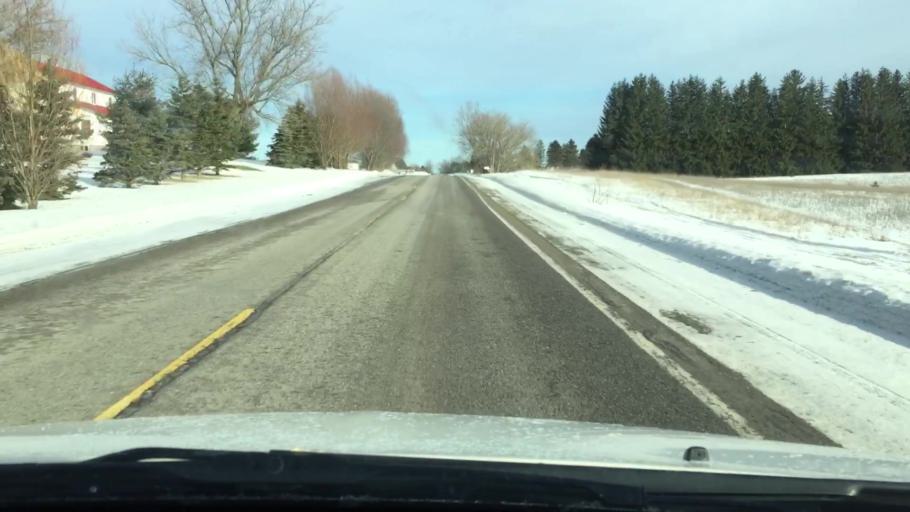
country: US
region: Michigan
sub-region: Kalkaska County
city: Kalkaska
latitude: 44.6404
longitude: -85.2027
